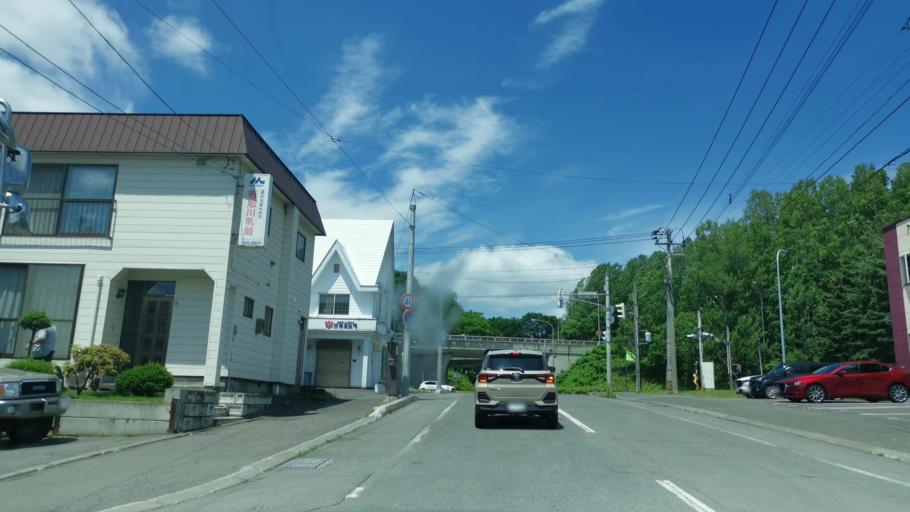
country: JP
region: Hokkaido
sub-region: Asahikawa-shi
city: Asahikawa
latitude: 43.7968
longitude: 142.3292
